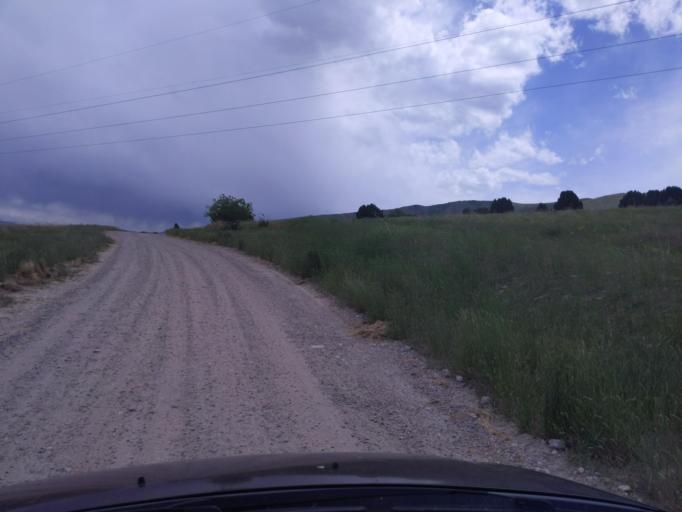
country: US
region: Idaho
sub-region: Bannock County
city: Pocatello
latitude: 42.8470
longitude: -112.4598
